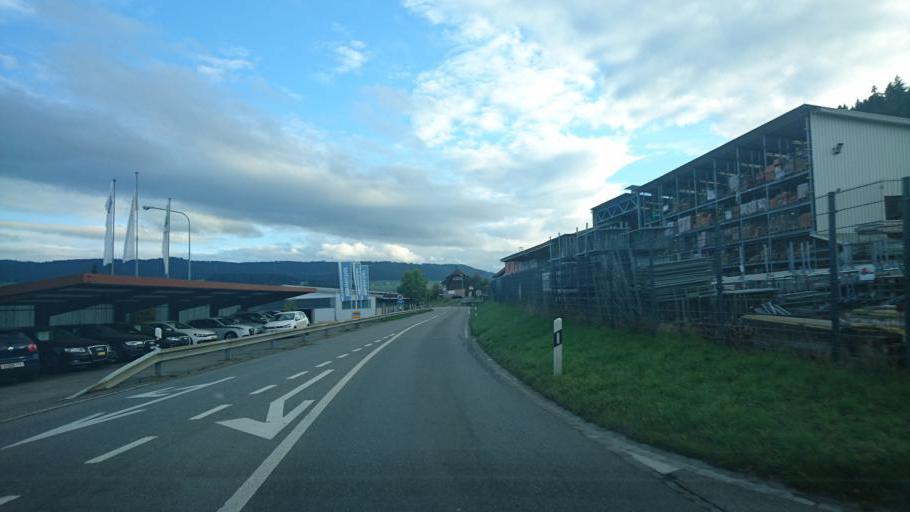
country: CH
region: Bern
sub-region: Bern-Mittelland District
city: Konolfingen
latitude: 46.8999
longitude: 7.6334
